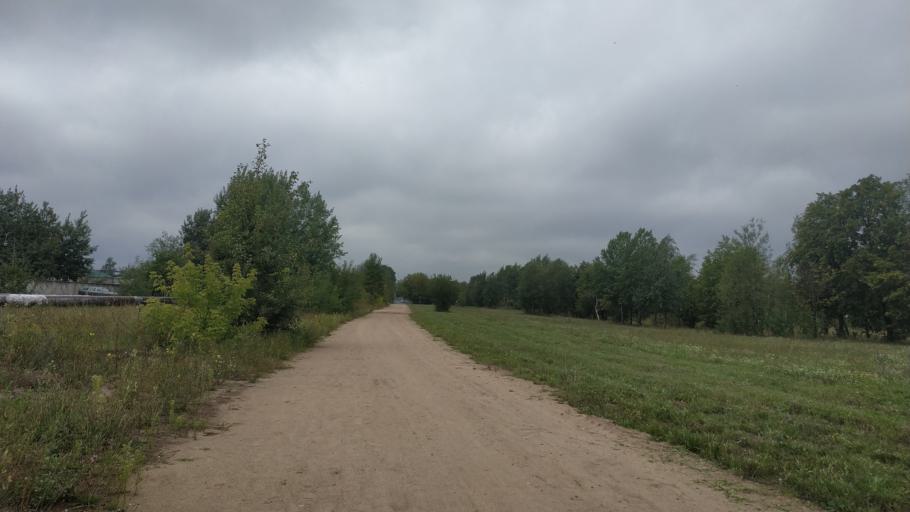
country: BY
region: Mogilev
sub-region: Mahilyowski Rayon
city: Veyno
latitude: 53.8596
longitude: 30.3321
